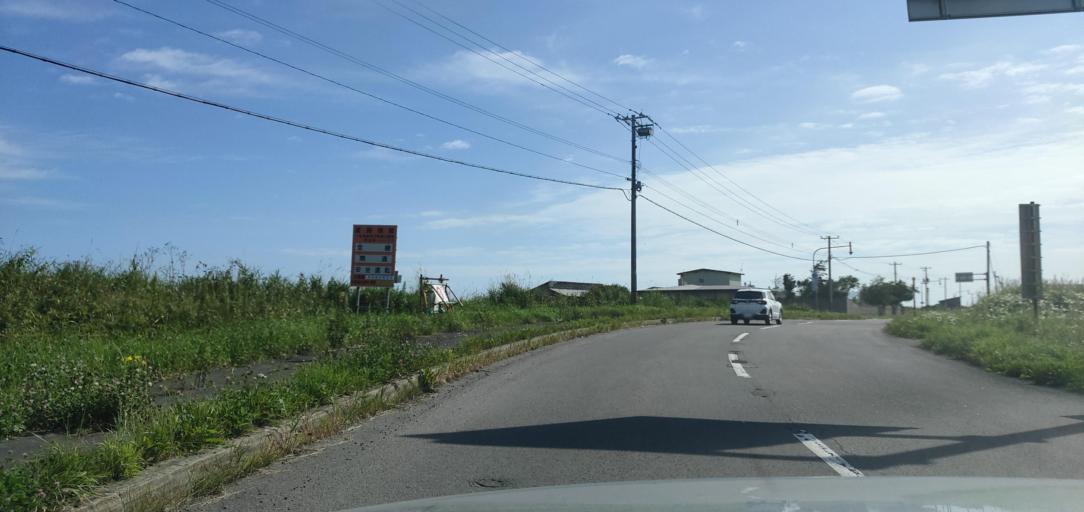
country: JP
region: Hokkaido
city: Shibetsu
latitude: 43.6384
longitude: 145.1634
